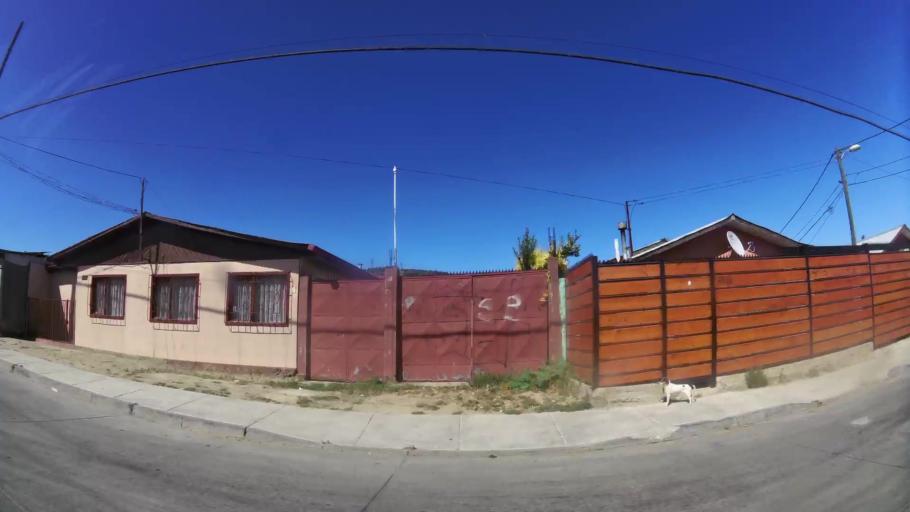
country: CL
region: Valparaiso
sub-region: Provincia de Valparaiso
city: Valparaiso
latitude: -33.0661
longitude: -71.5843
